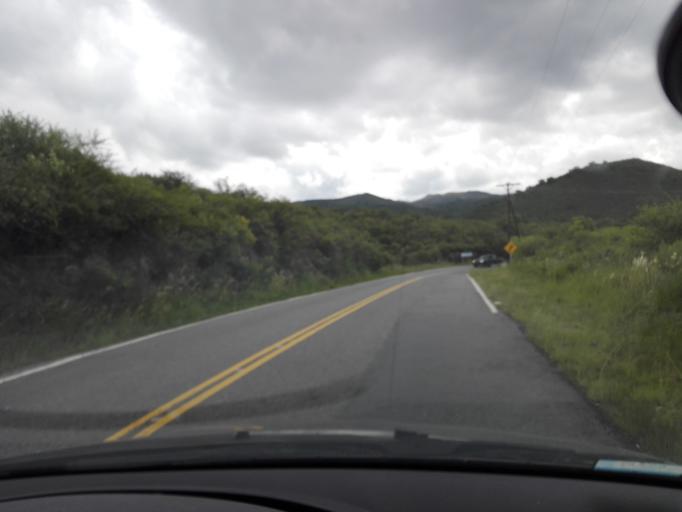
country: AR
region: Cordoba
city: Alta Gracia
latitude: -31.5967
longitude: -64.4912
